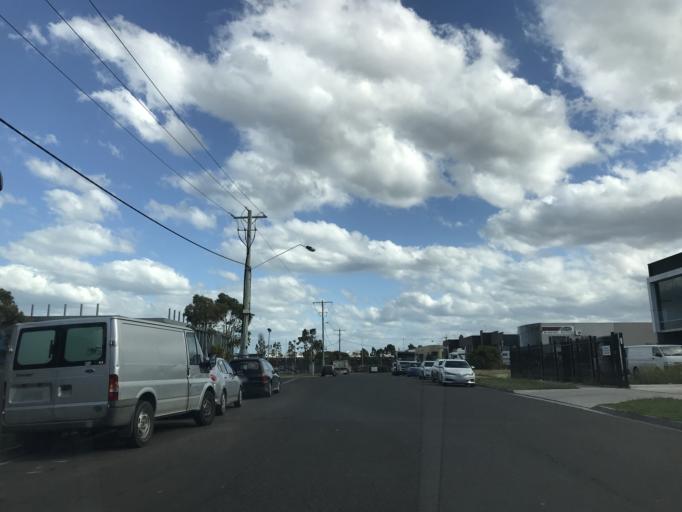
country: AU
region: Victoria
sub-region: Brimbank
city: Sunshine West
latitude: -37.8050
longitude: 144.8154
